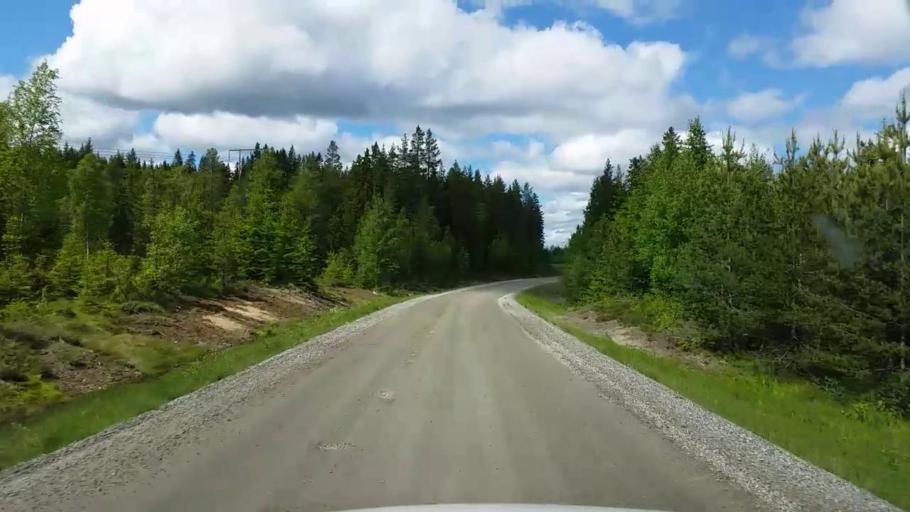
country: SE
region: Gaevleborg
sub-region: Bollnas Kommun
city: Vittsjo
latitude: 61.1740
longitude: 16.1522
